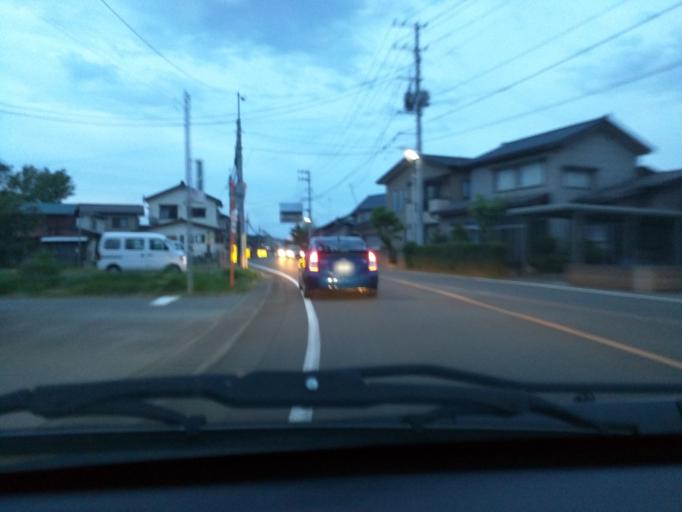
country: JP
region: Niigata
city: Kashiwazaki
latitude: 37.3381
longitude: 138.6166
